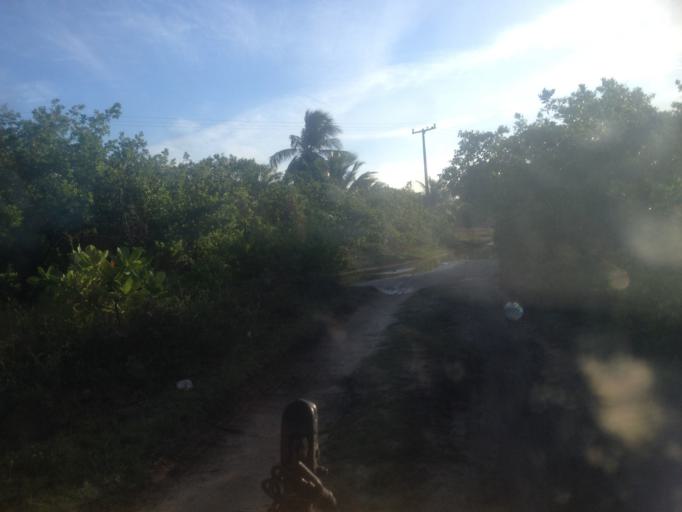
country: BR
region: Sergipe
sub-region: Indiaroba
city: Indiaroba
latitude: -11.4647
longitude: -37.3587
